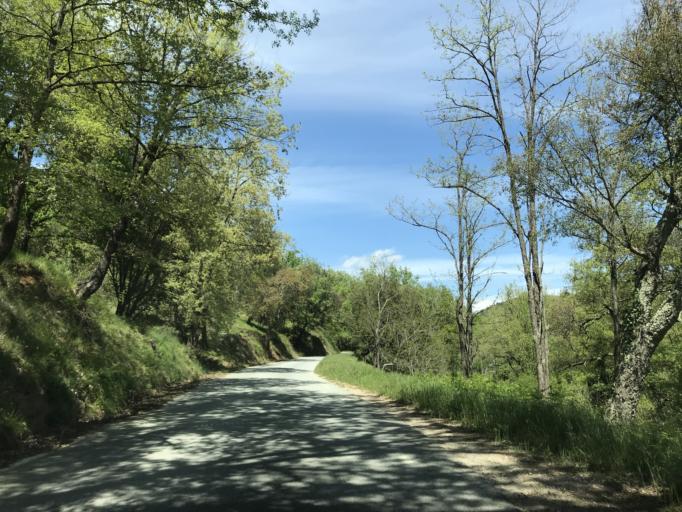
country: FR
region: Provence-Alpes-Cote d'Azur
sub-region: Departement du Var
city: Tanneron
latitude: 43.5797
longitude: 6.8218
